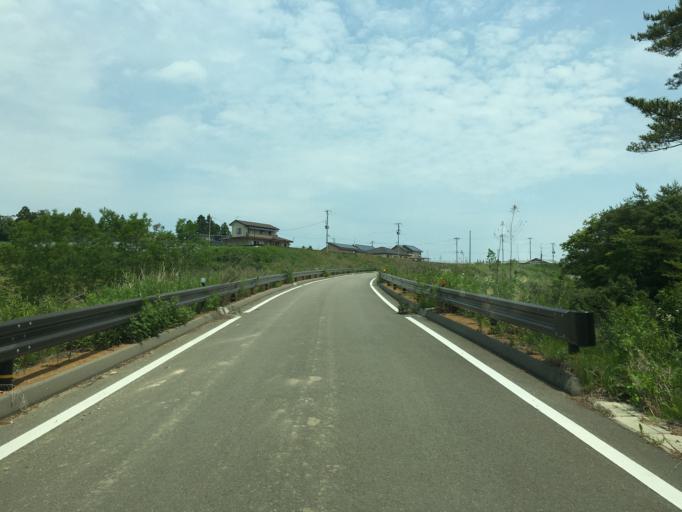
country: JP
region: Miyagi
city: Marumori
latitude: 37.7598
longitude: 140.9840
